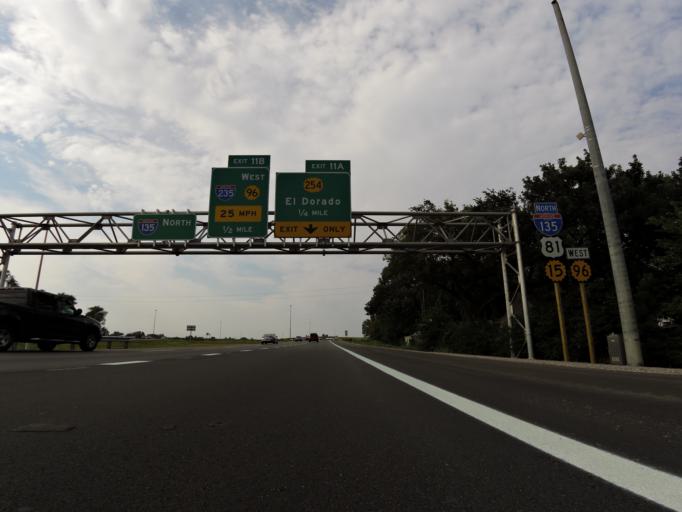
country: US
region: Kansas
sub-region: Sedgwick County
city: Park City
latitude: 37.7553
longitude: -97.3199
